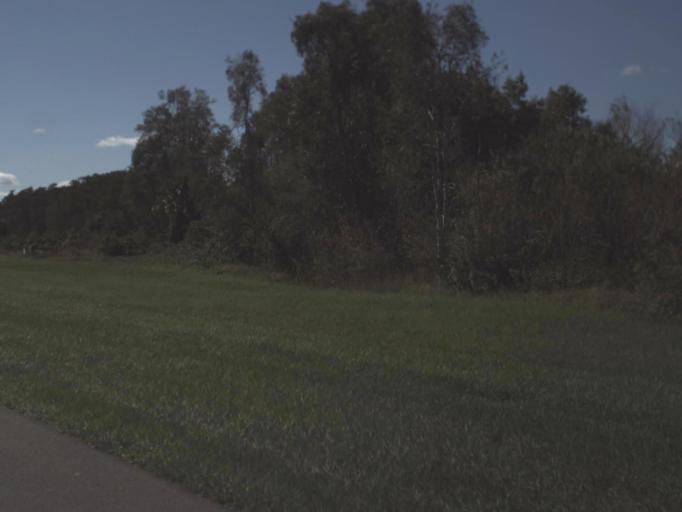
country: US
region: Florida
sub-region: Lee County
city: Lehigh Acres
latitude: 26.5418
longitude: -81.6353
